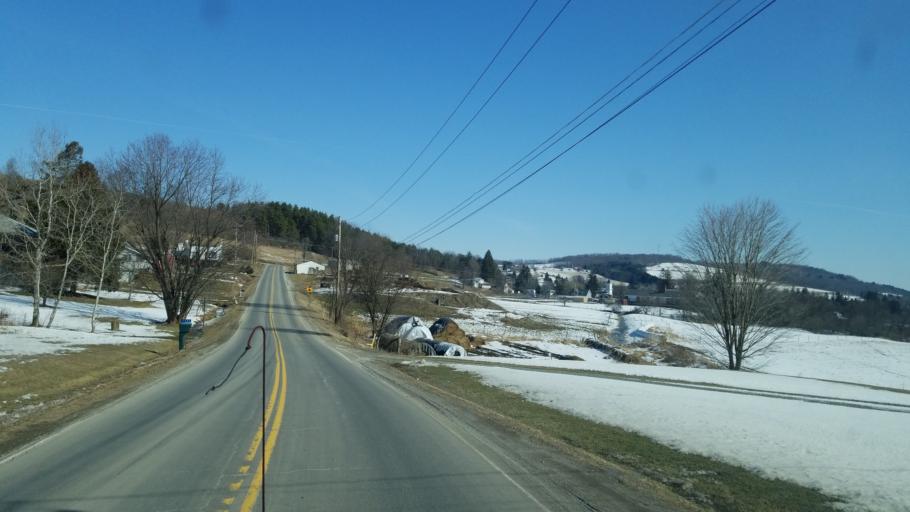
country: US
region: Pennsylvania
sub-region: Tioga County
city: Elkland
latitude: 42.0769
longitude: -77.4188
